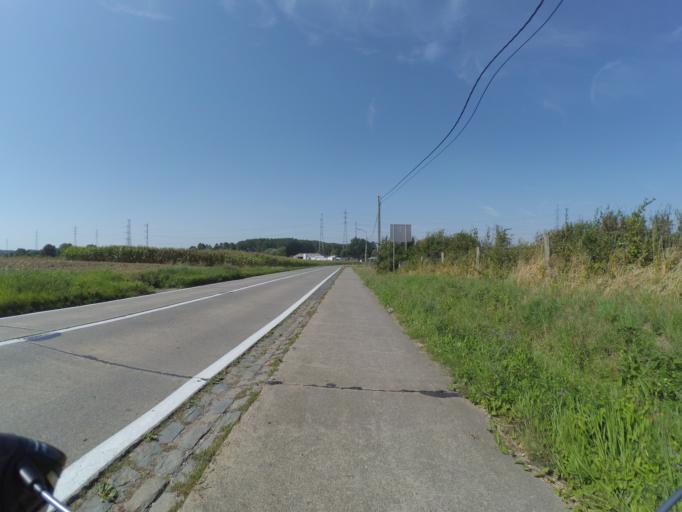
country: BE
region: Flanders
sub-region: Provincie West-Vlaanderen
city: Anzegem
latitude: 50.8589
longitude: 3.4902
